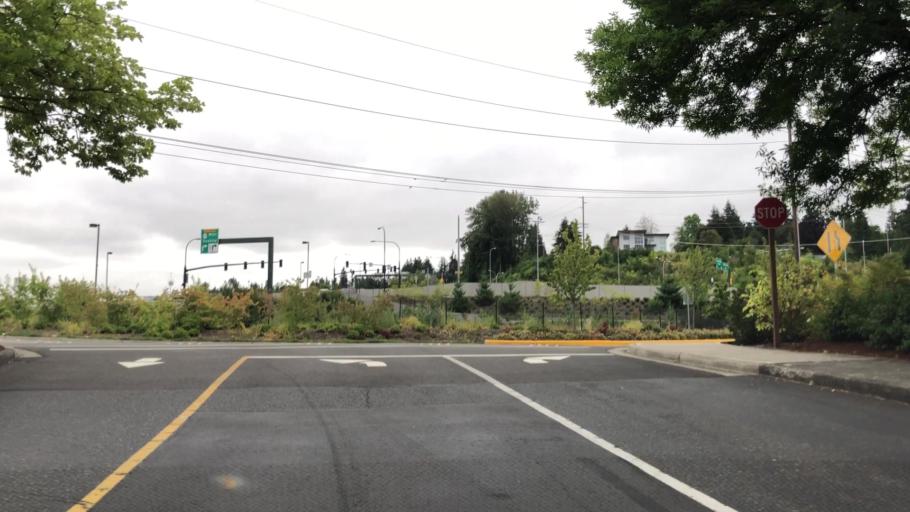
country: US
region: Washington
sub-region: King County
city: Yarrow Point
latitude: 47.6442
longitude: -122.2026
